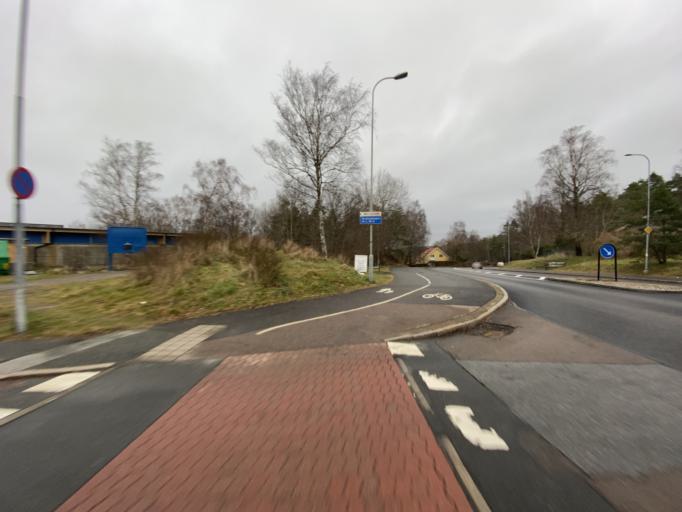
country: SE
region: Vaestra Goetaland
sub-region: Goteborg
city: Eriksbo
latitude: 57.7148
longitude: 12.0395
